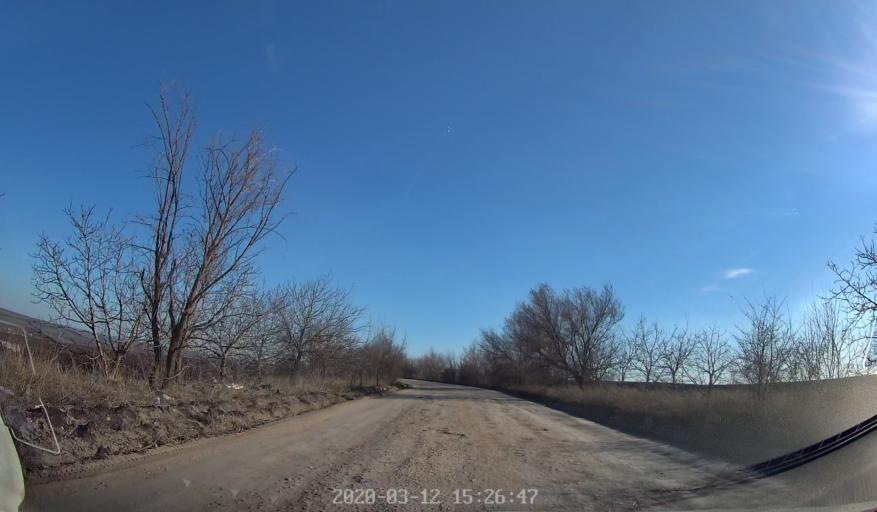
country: MD
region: Chisinau
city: Ciorescu
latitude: 47.1760
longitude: 28.9239
